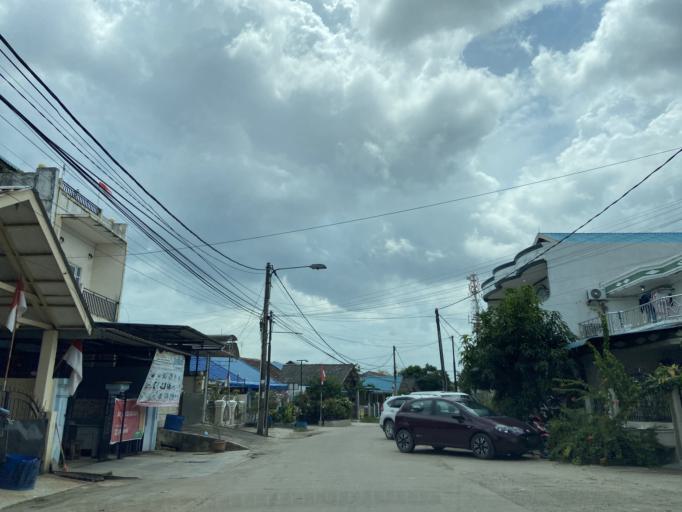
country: SG
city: Singapore
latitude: 1.1250
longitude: 104.0117
